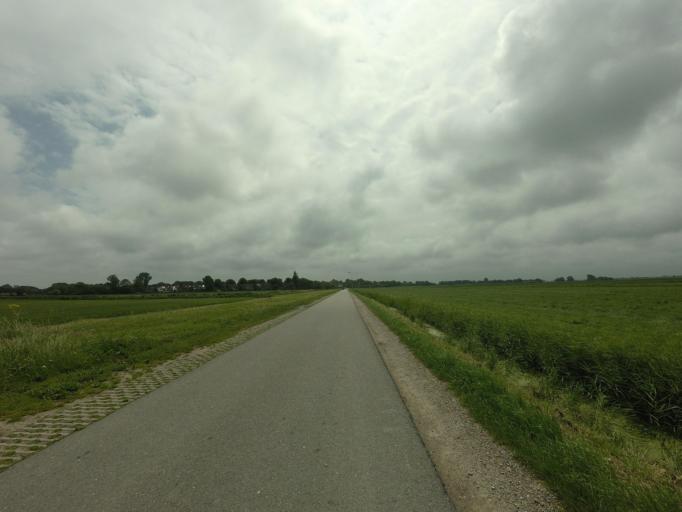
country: NL
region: North Holland
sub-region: Gemeente Schagen
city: Schagen
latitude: 52.7890
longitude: 4.7711
